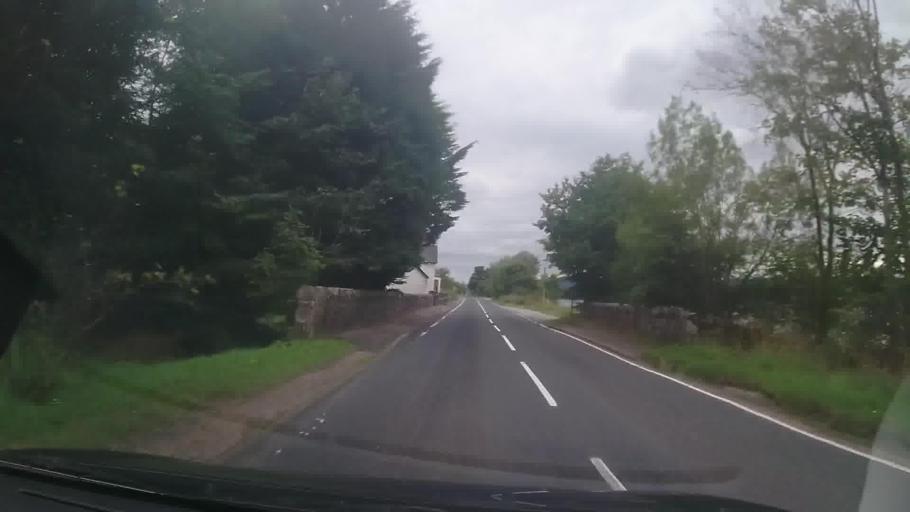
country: GB
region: Scotland
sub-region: Argyll and Bute
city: Garelochhead
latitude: 56.2236
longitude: -5.0294
